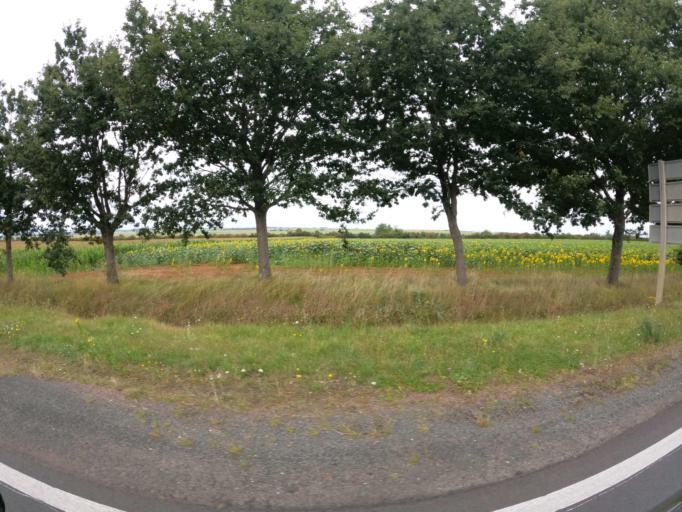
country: FR
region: Pays de la Loire
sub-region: Departement de la Vendee
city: Saint-Michel-le-Cloucq
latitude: 46.4436
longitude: -0.7561
